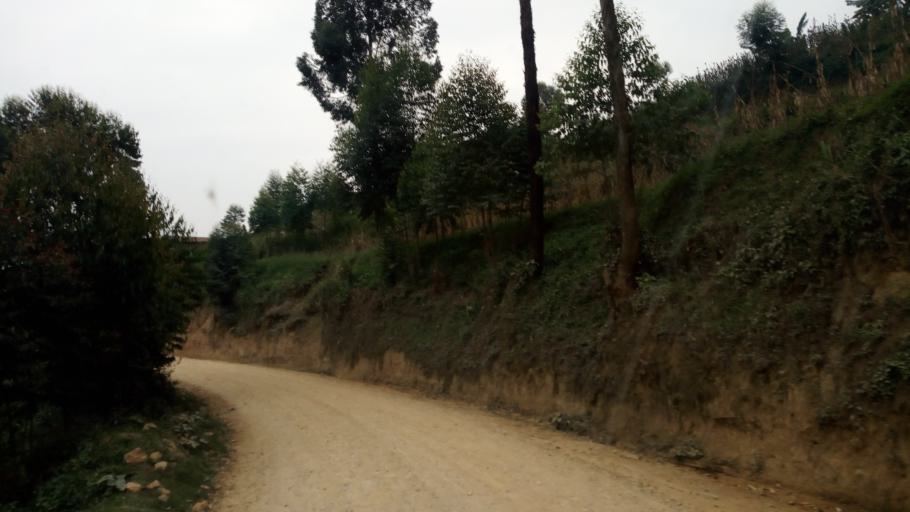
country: UG
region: Western Region
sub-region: Kanungu District
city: Kanungu
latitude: -1.1083
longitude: 29.8648
